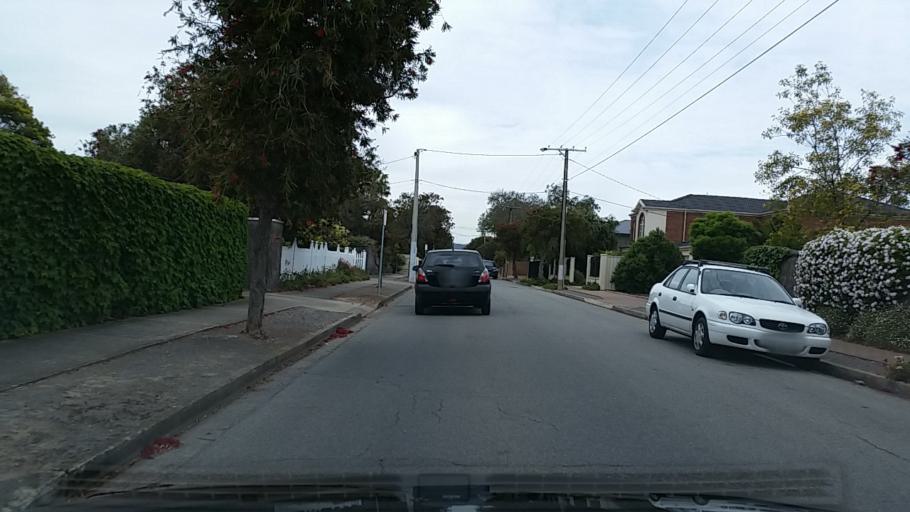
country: AU
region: South Australia
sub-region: Holdfast Bay
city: North Brighton
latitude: -35.0089
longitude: 138.5192
